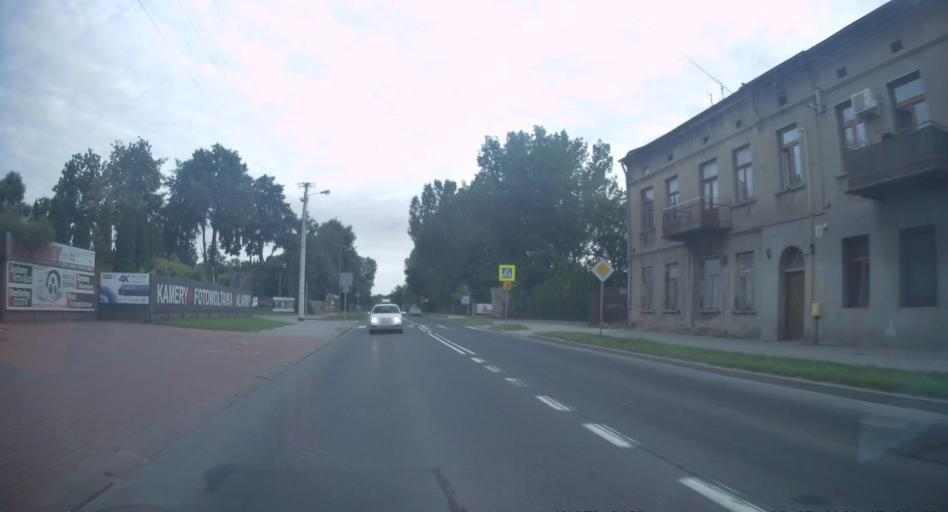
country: PL
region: Lodz Voivodeship
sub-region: Powiat radomszczanski
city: Radomsko
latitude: 51.0734
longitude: 19.4472
